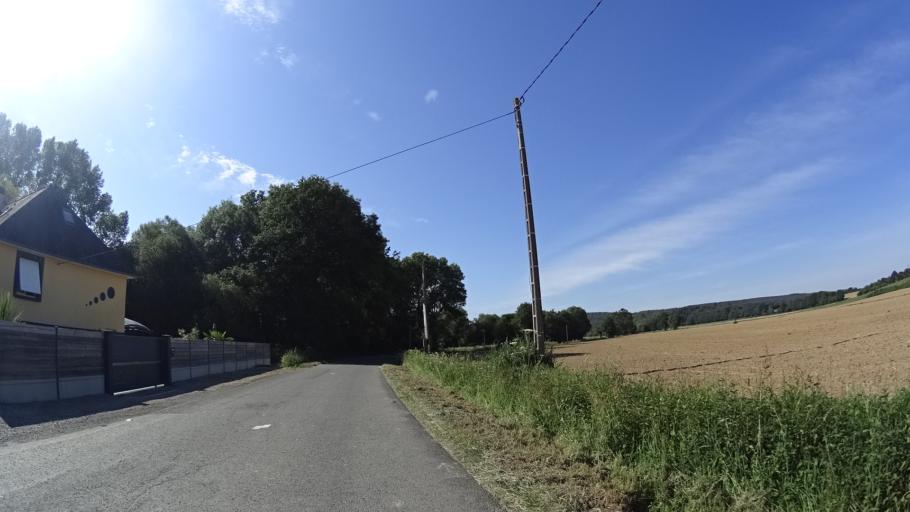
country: FR
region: Brittany
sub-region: Departement d'Ille-et-Vilaine
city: Guipry
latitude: 47.7939
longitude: -1.8482
